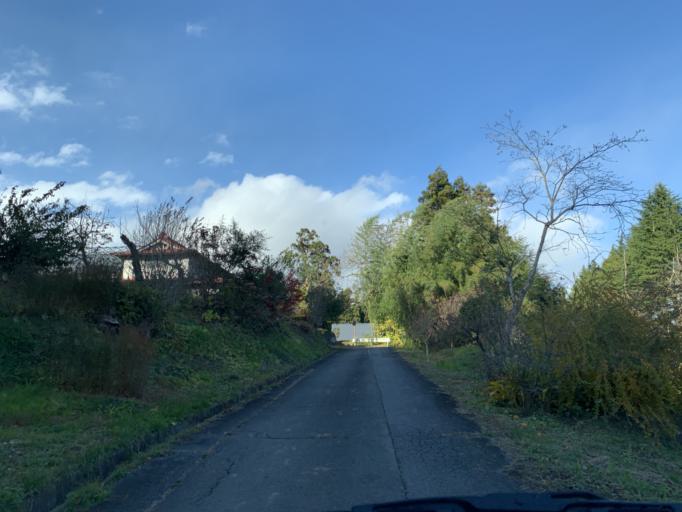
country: JP
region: Iwate
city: Ichinoseki
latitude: 39.0096
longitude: 141.0870
